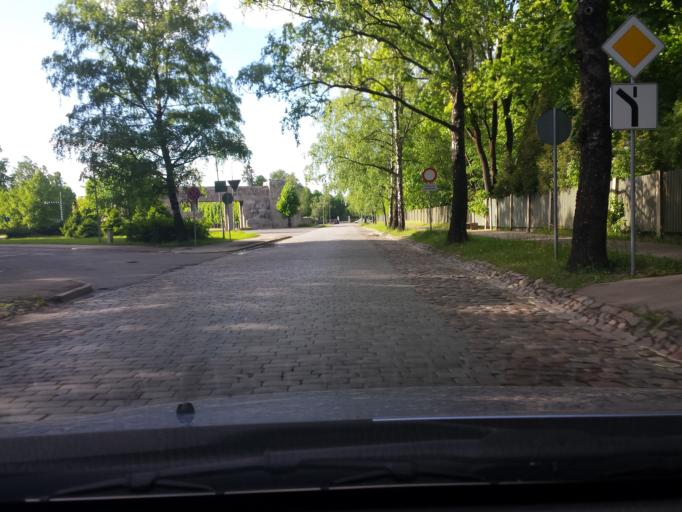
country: LV
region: Riga
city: Riga
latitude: 56.9846
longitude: 24.1481
